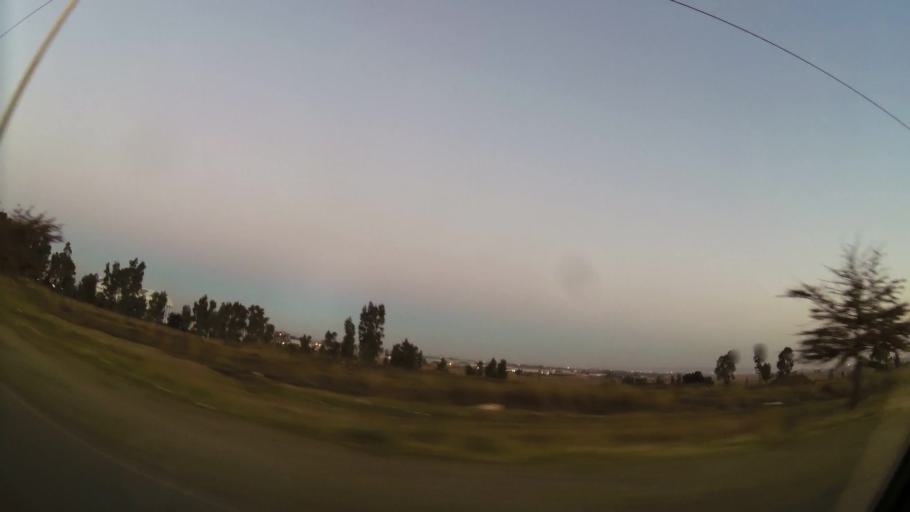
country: ZA
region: Gauteng
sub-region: Ekurhuleni Metropolitan Municipality
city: Germiston
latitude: -26.2813
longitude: 28.1696
